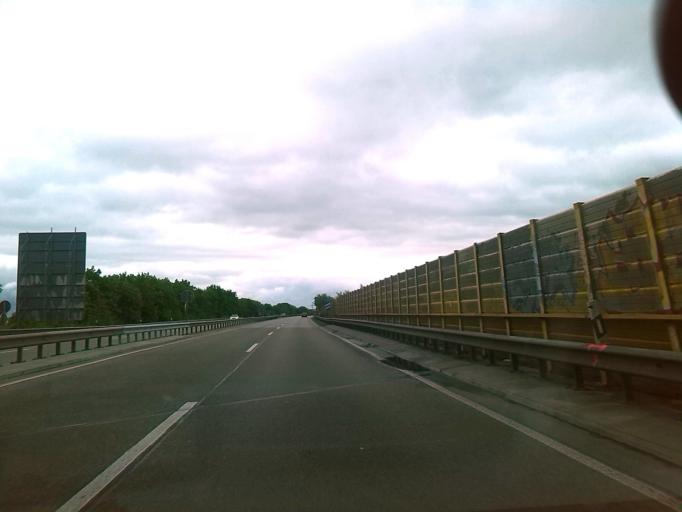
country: DE
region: Rheinland-Pfalz
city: Maxdorf
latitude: 49.4794
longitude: 8.3209
